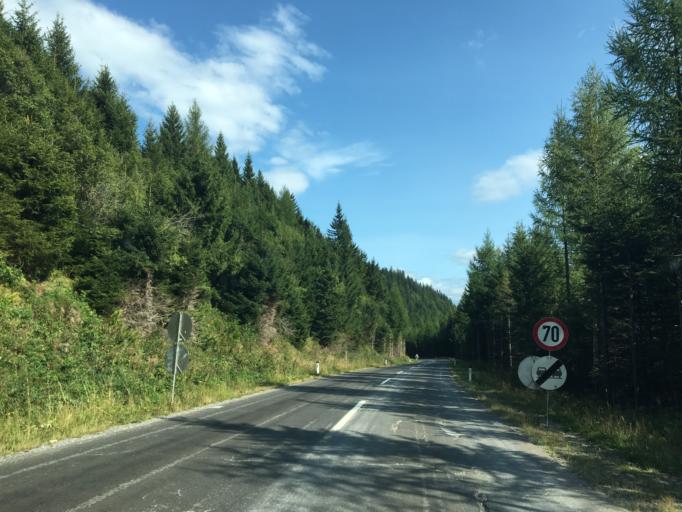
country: AT
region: Styria
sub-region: Politischer Bezirk Deutschlandsberg
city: Kloster
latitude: 46.8353
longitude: 15.0285
